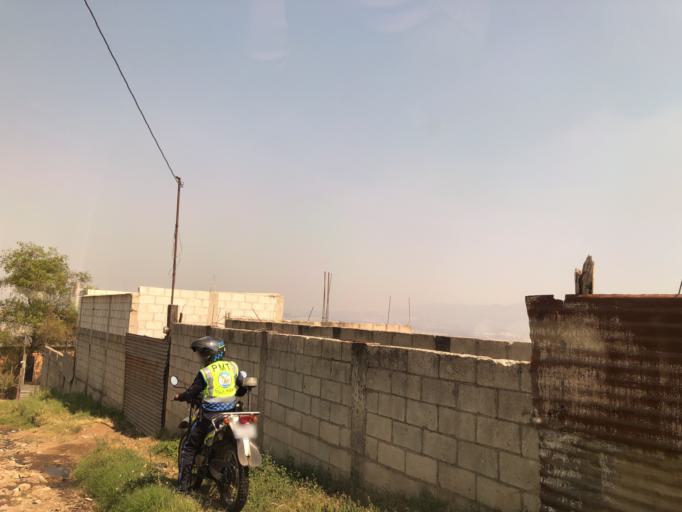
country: GT
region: Guatemala
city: Villa Nueva
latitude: 14.5008
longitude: -90.5915
